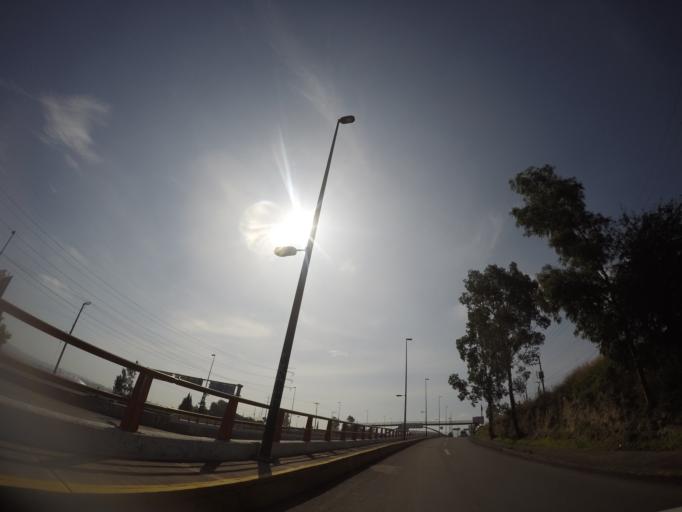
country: MX
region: Michoacan
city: Morelia
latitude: 19.7240
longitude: -101.1948
